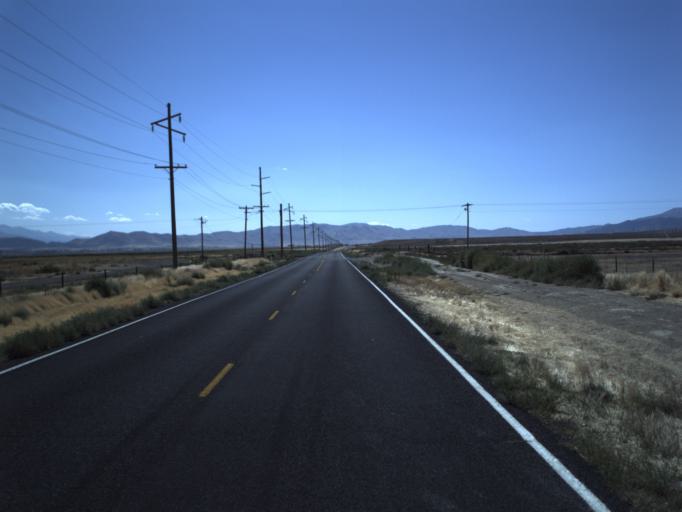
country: US
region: Utah
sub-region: Utah County
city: Genola
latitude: 40.0559
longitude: -111.9584
